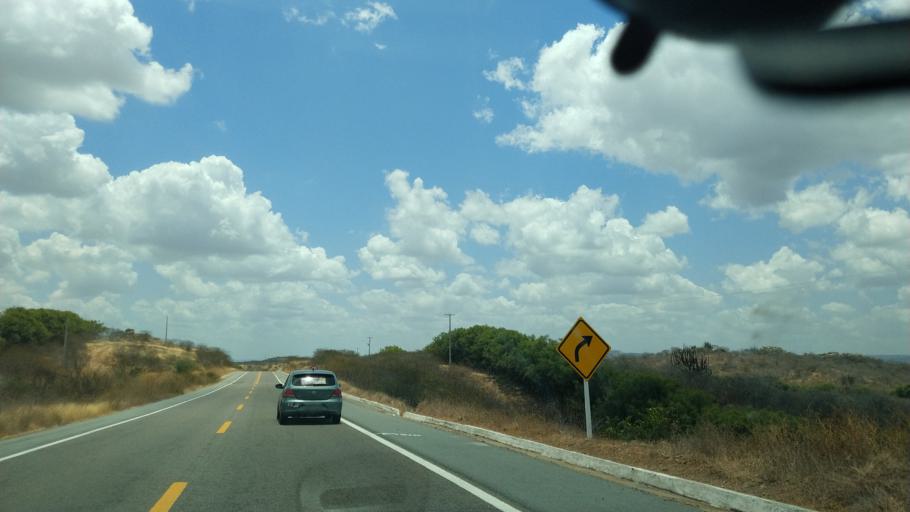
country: BR
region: Rio Grande do Norte
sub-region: Cerro Cora
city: Cerro Cora
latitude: -6.2089
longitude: -36.3114
